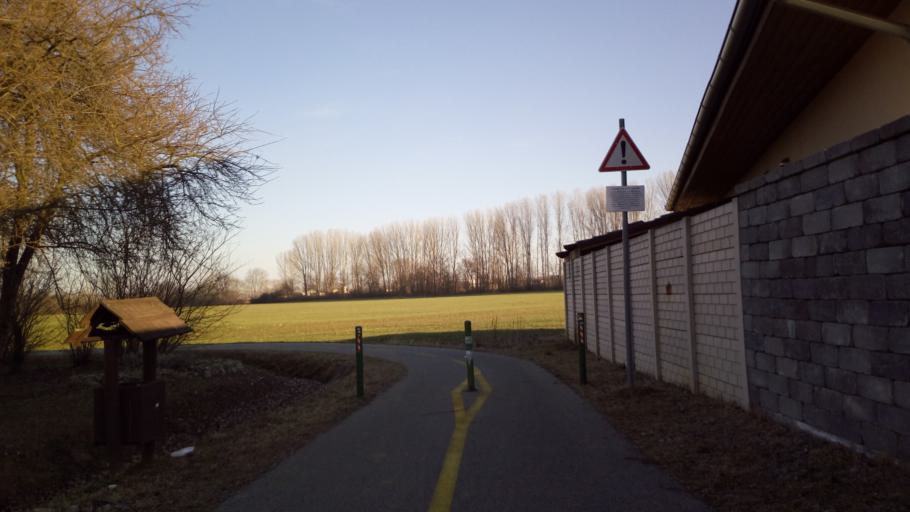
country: HU
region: Baranya
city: Pellerd
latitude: 46.0341
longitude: 18.1665
